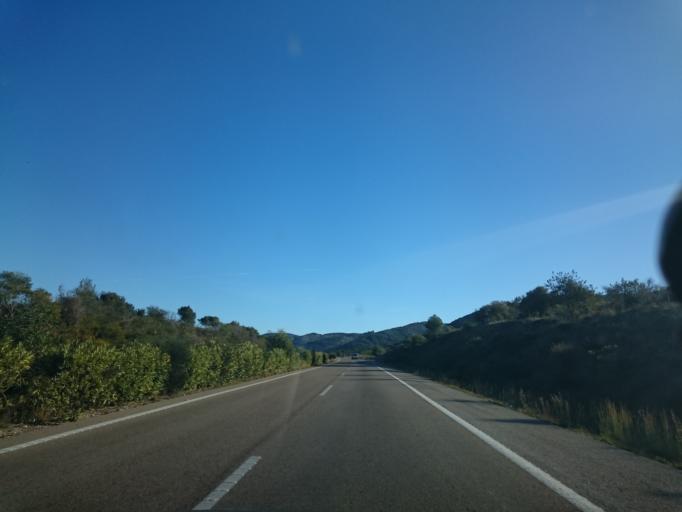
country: ES
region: Valencia
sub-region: Provincia de Castello
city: Santa Magdalena de Pulpis
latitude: 40.3459
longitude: 0.2847
